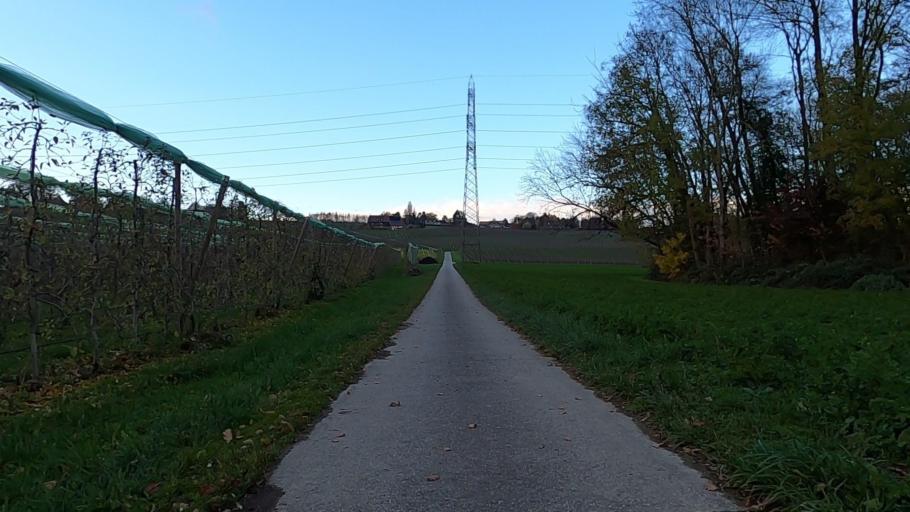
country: CH
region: Vaud
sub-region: Morges District
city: Morges
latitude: 46.5162
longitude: 6.4685
